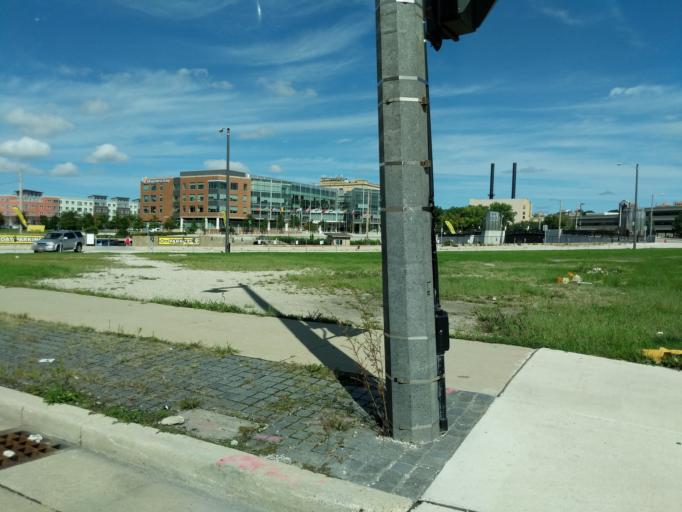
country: US
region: Wisconsin
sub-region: Milwaukee County
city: Milwaukee
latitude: 43.0471
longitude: -87.9114
